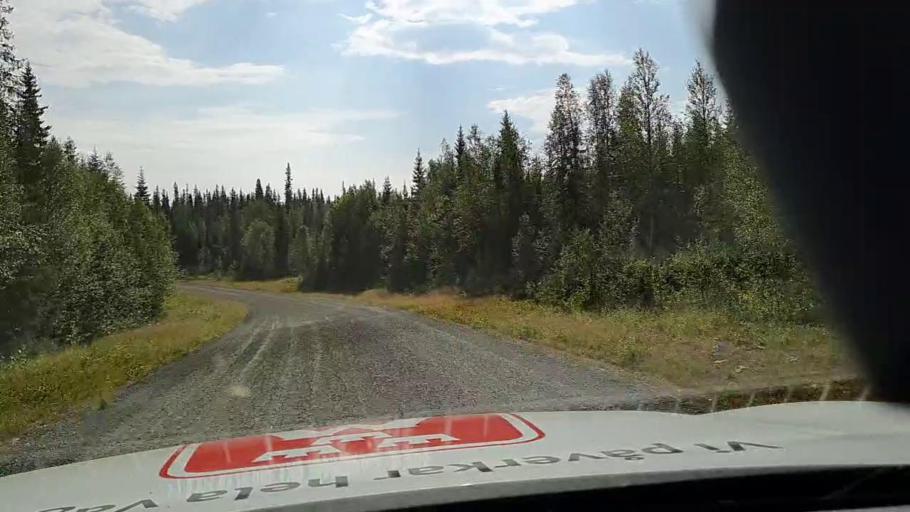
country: SE
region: Vaesterbotten
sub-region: Storumans Kommun
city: Fristad
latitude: 65.5409
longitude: 16.7988
